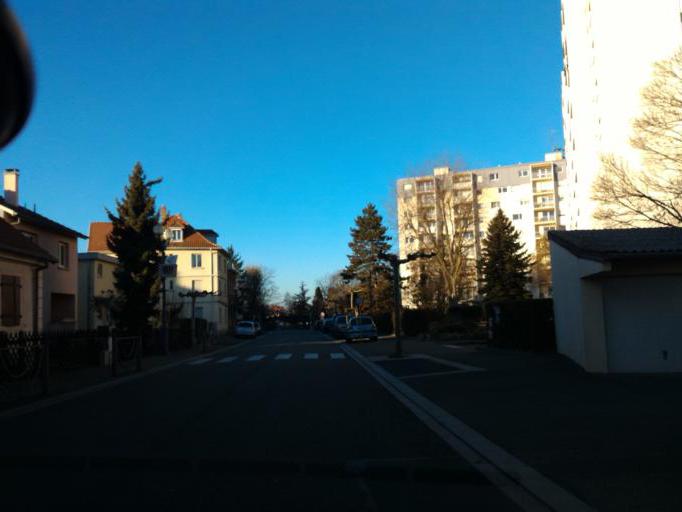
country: FR
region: Alsace
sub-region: Departement du Haut-Rhin
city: Riedisheim
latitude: 47.7525
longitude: 7.3690
